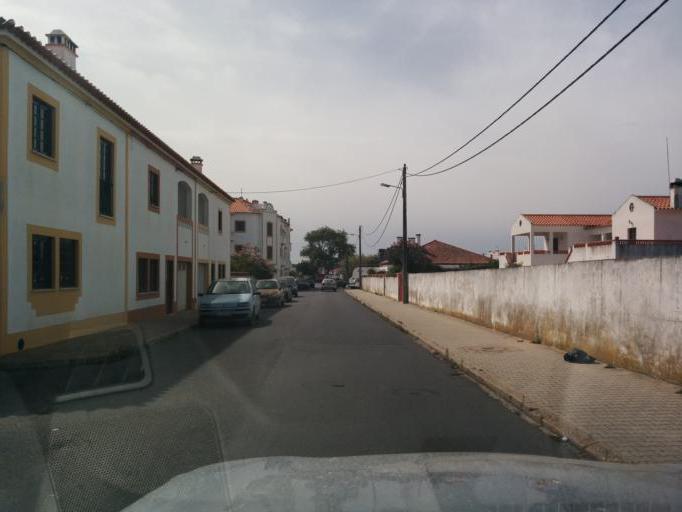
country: PT
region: Beja
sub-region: Odemira
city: Vila Nova de Milfontes
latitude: 37.7270
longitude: -8.7848
